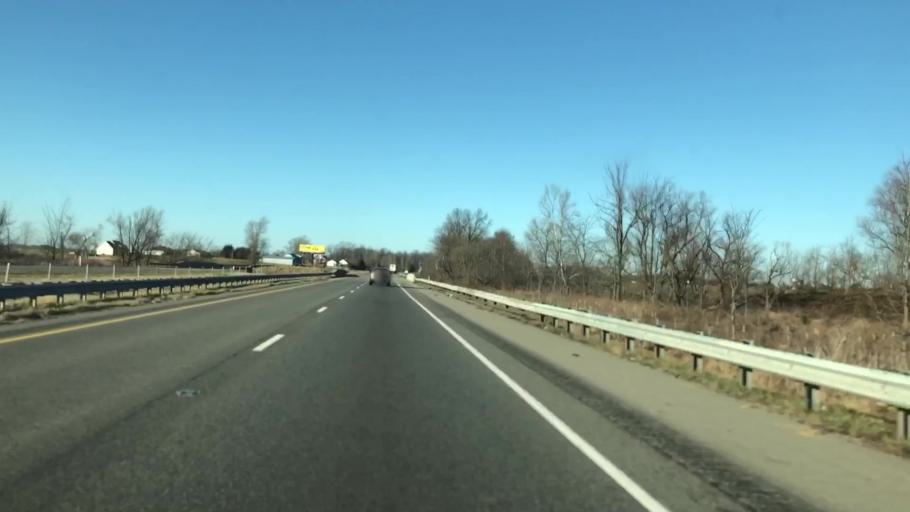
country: US
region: Indiana
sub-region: Jackson County
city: Seymour
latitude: 38.9322
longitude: -85.8406
